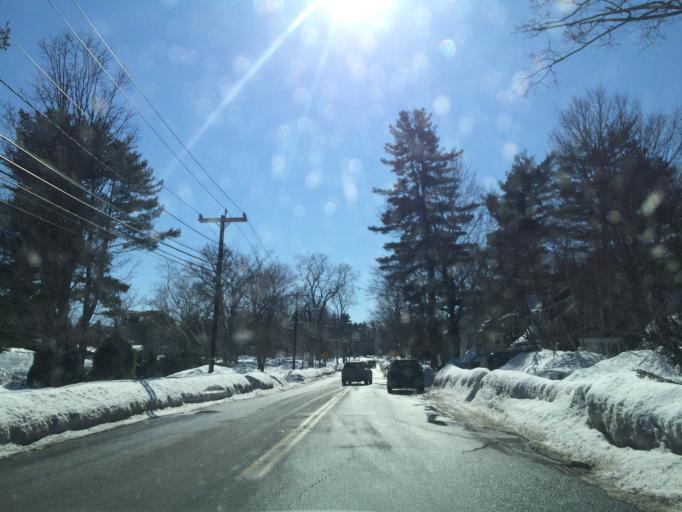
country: US
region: Massachusetts
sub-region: Norfolk County
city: Wellesley
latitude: 42.2895
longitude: -71.2898
